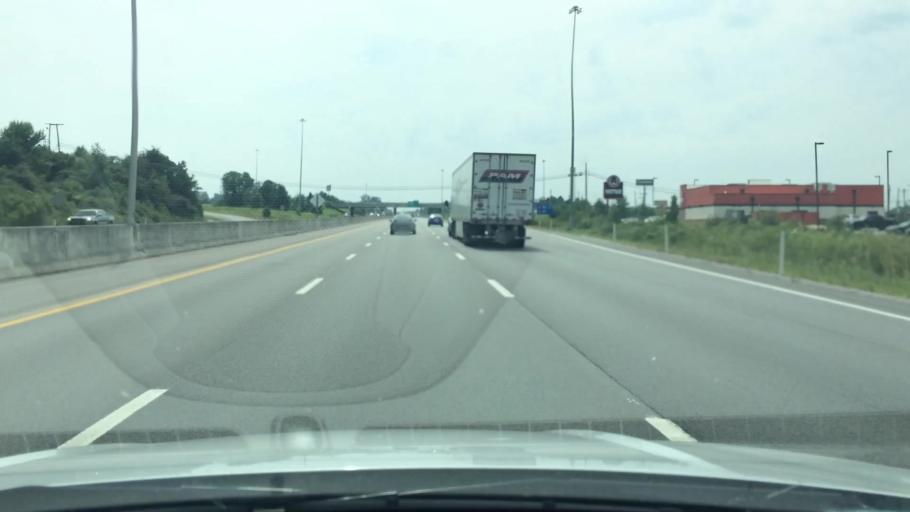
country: US
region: Kentucky
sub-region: Laurel County
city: London
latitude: 37.1511
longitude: -84.1121
